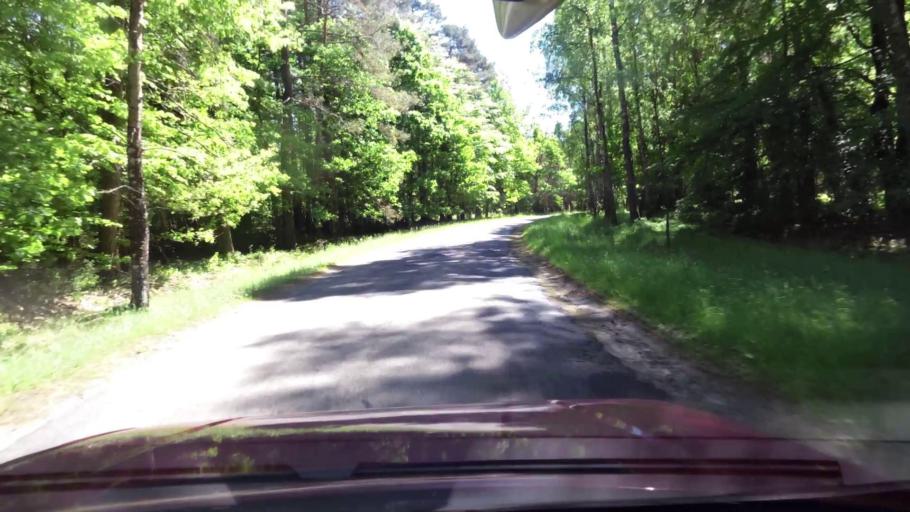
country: PL
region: West Pomeranian Voivodeship
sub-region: Powiat koszalinski
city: Bobolice
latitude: 54.0672
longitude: 16.5647
